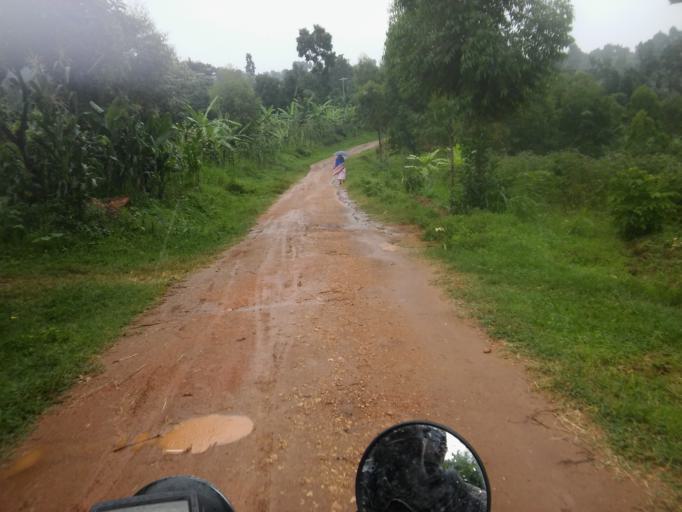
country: UG
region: Eastern Region
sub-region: Bududa District
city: Bududa
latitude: 0.9989
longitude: 34.2457
